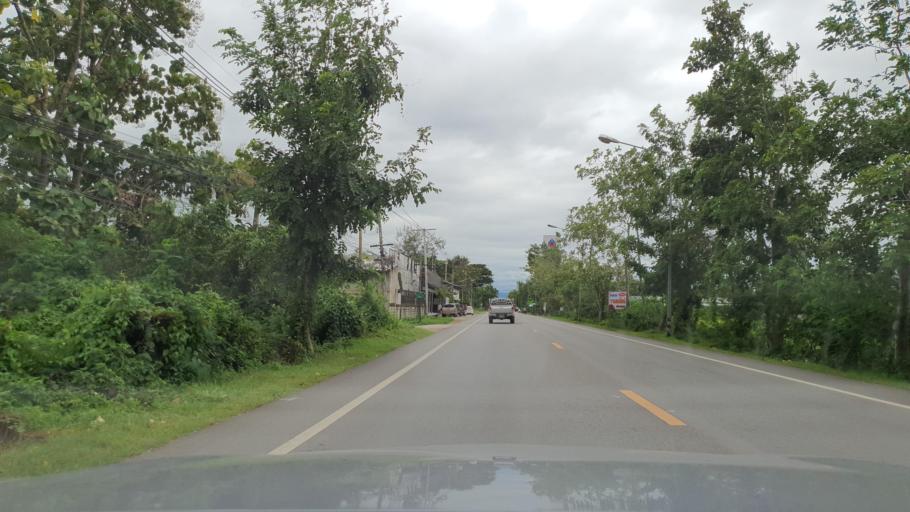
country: TH
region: Lamphun
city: Lamphun
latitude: 18.5870
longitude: 98.9873
